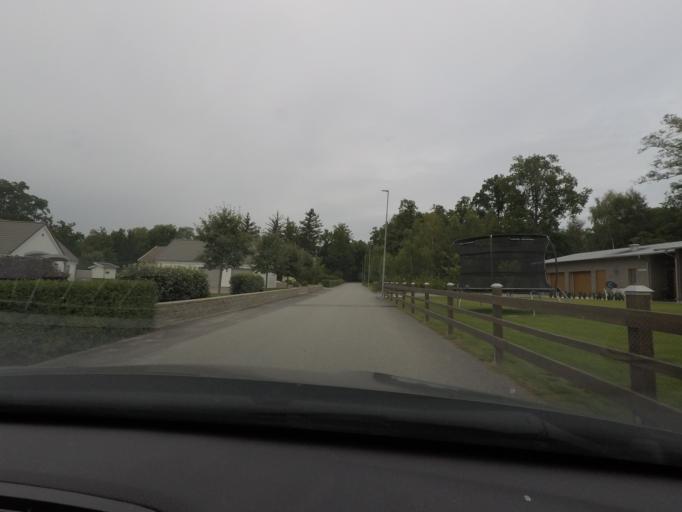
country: SE
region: Skane
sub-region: Osby Kommun
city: Osby
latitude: 56.3591
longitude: 13.9969
